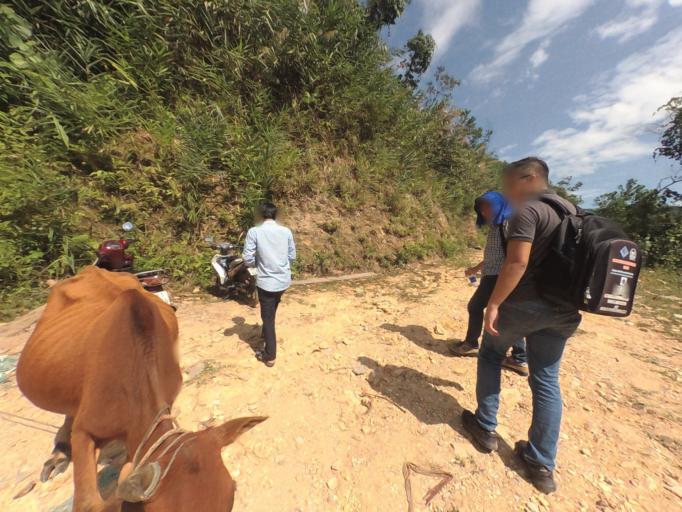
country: VN
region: Thua Thien-Hue
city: A Luoi
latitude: 16.3047
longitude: 107.3249
